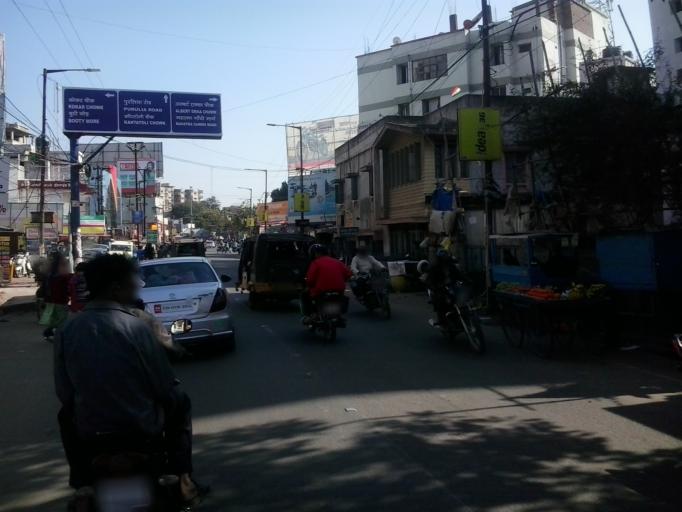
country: IN
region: Jharkhand
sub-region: Ranchi
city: Ranchi
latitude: 23.3733
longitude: 85.3369
